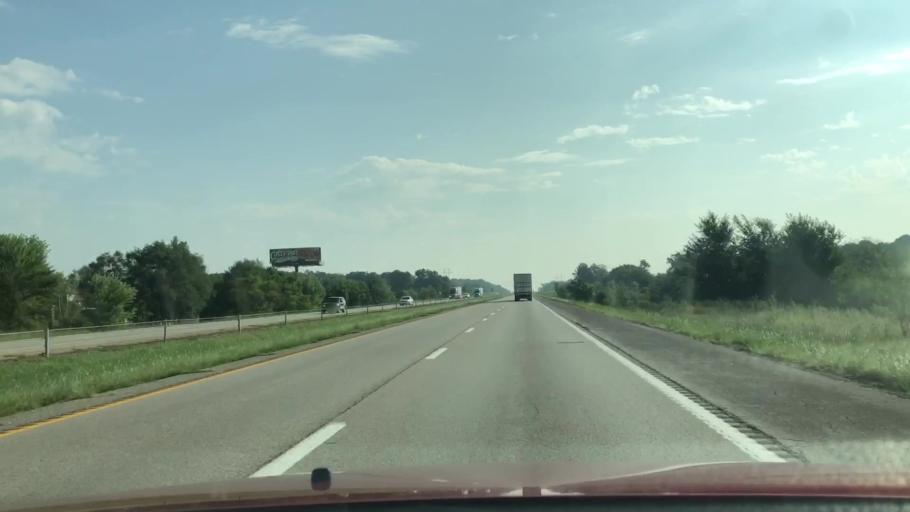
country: US
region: Missouri
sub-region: Laclede County
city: Lebanon
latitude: 37.5768
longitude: -92.7568
